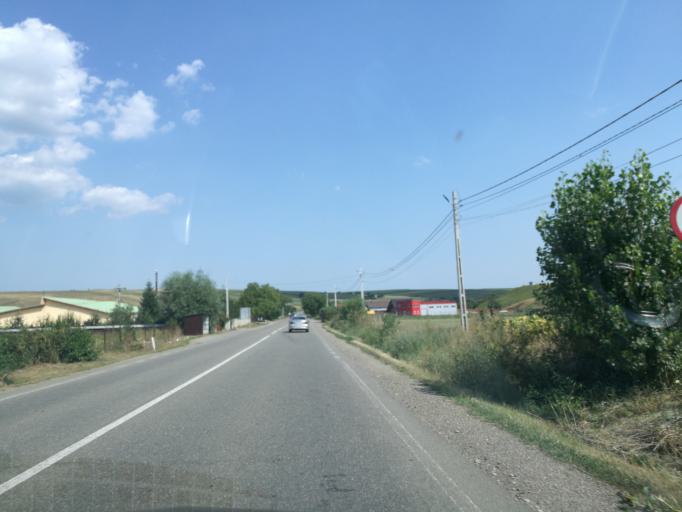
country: RO
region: Neamt
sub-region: Comuna Baltatesti
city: Valea Seaca
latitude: 47.1400
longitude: 26.3174
